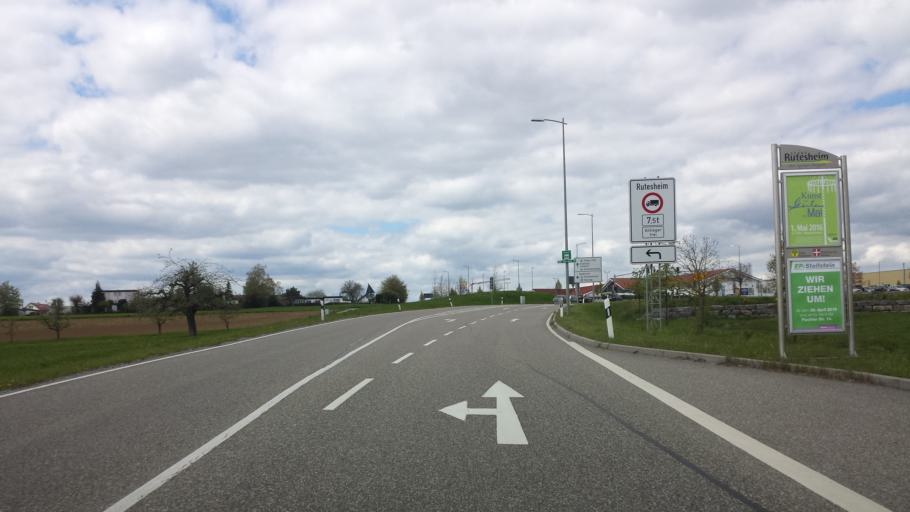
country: DE
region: Baden-Wuerttemberg
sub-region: Regierungsbezirk Stuttgart
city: Rutesheim
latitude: 48.8059
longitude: 8.9587
